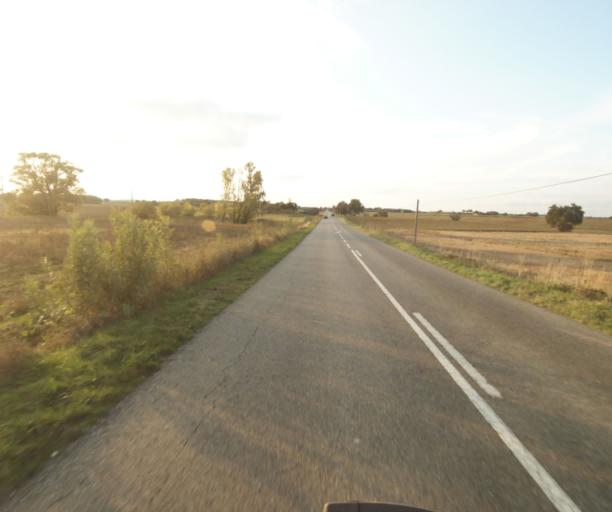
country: FR
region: Midi-Pyrenees
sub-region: Departement du Tarn-et-Garonne
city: Verdun-sur-Garonne
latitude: 43.8255
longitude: 1.1750
